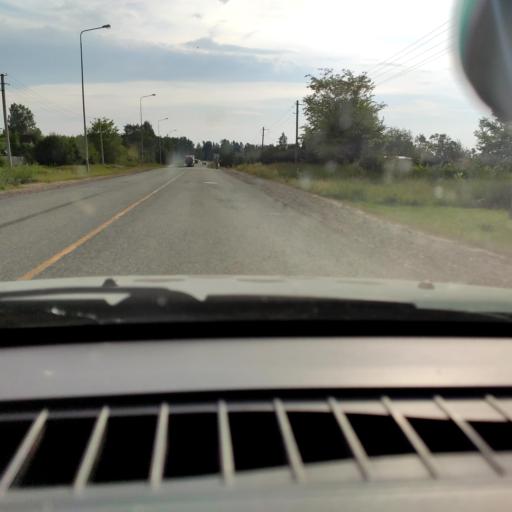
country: RU
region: Udmurtiya
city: Igra
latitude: 57.5738
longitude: 53.1336
